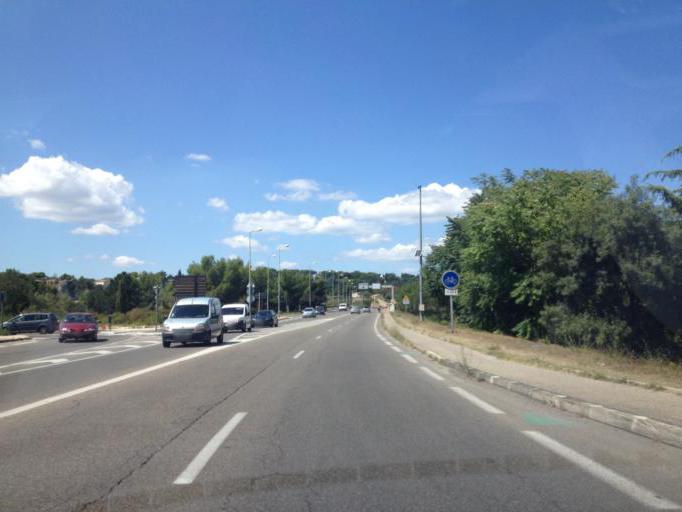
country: FR
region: Provence-Alpes-Cote d'Azur
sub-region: Departement du Vaucluse
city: Avignon
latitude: 43.9526
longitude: 4.7963
